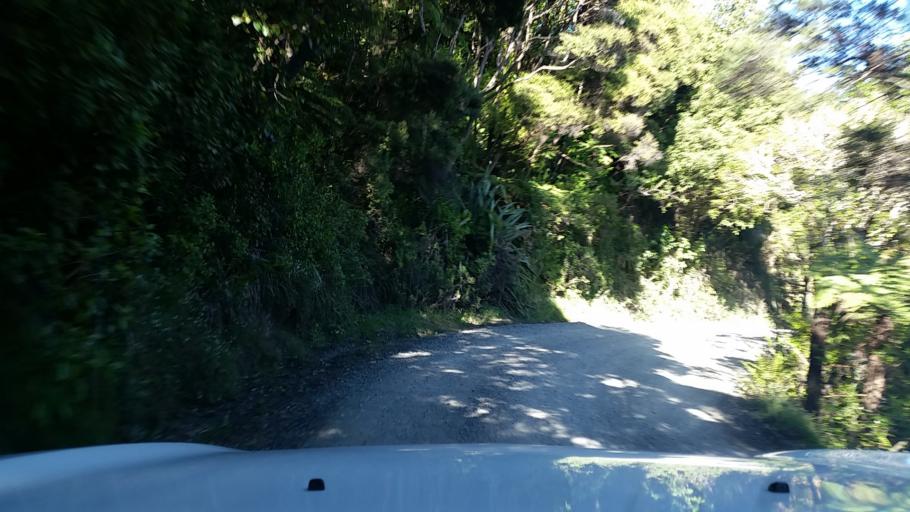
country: NZ
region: Auckland
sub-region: Auckland
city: Titirangi
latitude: -37.0306
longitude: 174.5239
